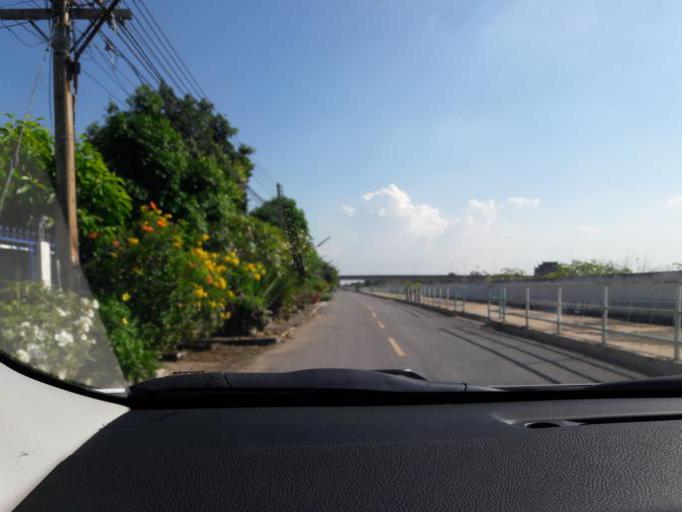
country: TH
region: Ang Thong
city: Ang Thong
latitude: 14.5797
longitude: 100.4481
